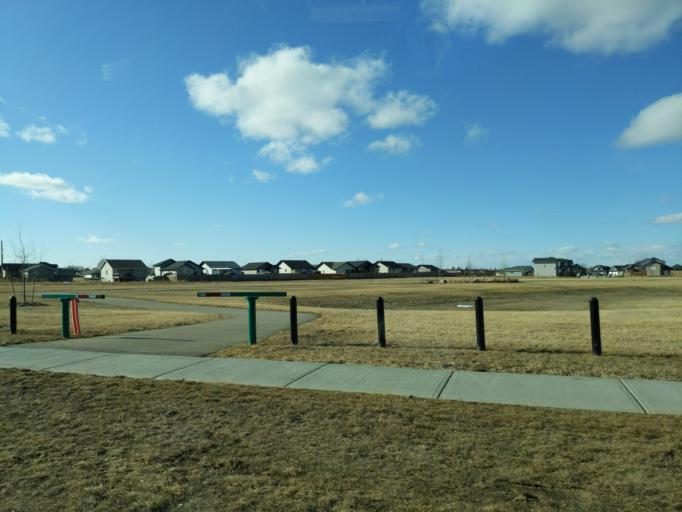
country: CA
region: Saskatchewan
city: Lloydminster
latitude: 53.2662
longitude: -109.9826
